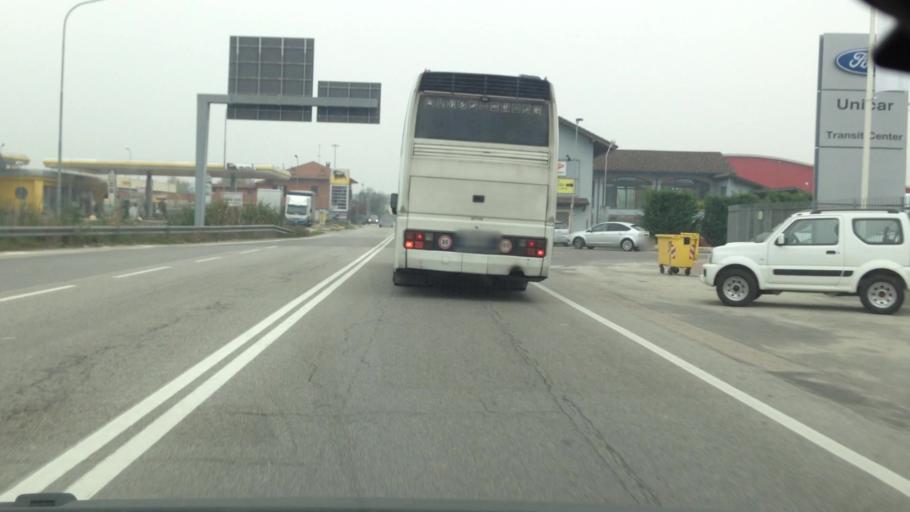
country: IT
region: Piedmont
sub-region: Provincia di Asti
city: Azzano d'Asti
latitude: 44.9063
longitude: 8.2500
